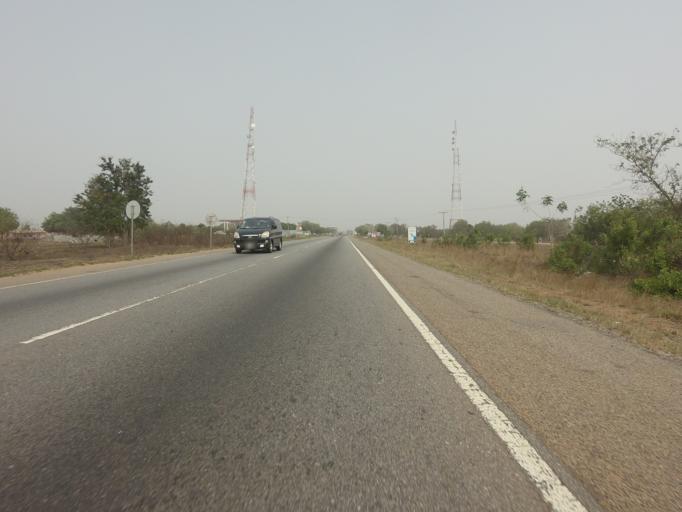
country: GH
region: Greater Accra
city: Tema
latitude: 5.8645
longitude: 0.2866
